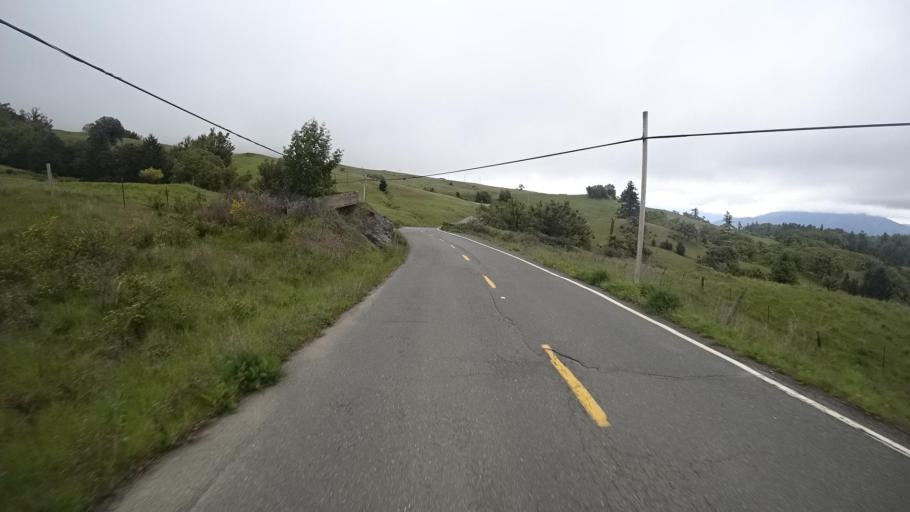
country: US
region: California
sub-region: Humboldt County
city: Redway
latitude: 40.1103
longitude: -123.7176
